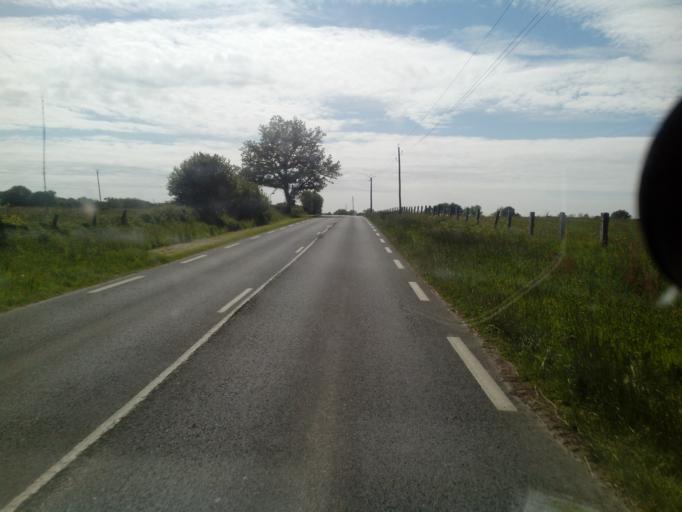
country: FR
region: Lower Normandy
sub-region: Departement du Calvados
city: Touques
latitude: 49.2595
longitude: 0.0975
